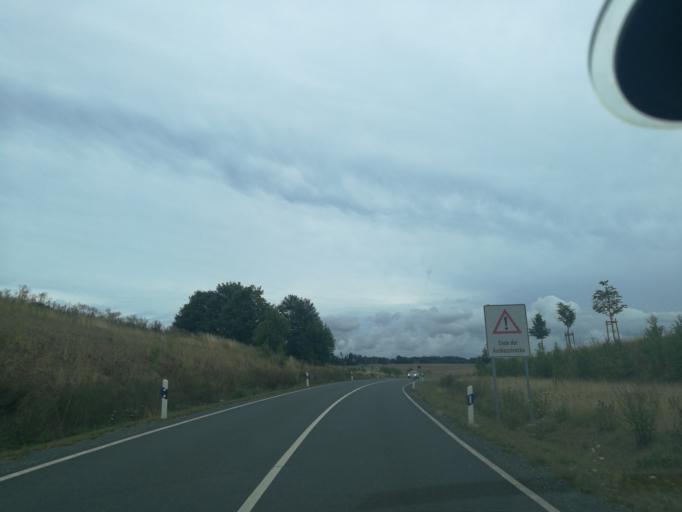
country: DE
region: Saxony
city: Triebel
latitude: 50.3352
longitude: 12.0868
